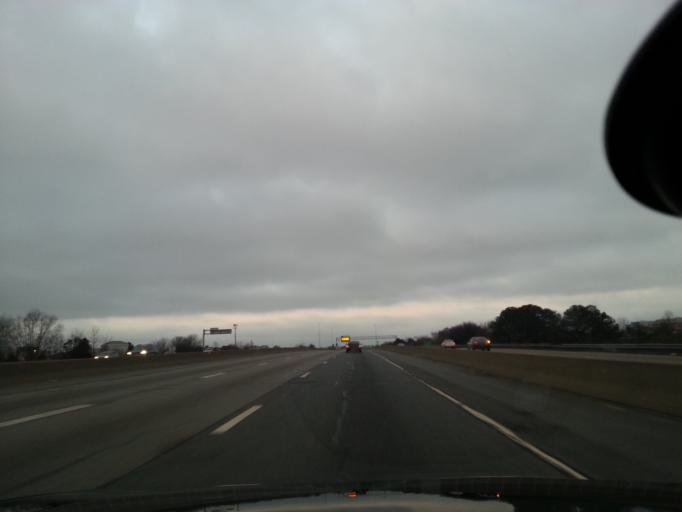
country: US
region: Virginia
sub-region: City of Chesapeake
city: Chesapeake
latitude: 36.8461
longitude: -76.1808
